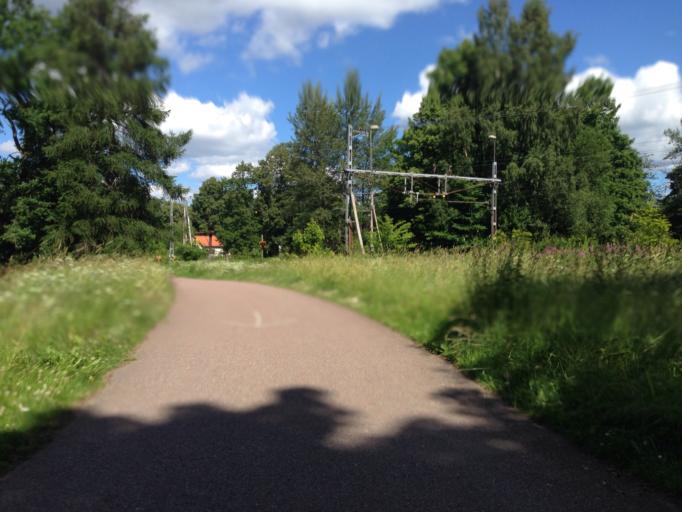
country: SE
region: Dalarna
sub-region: Ludvika Kommun
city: Ludvika
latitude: 60.1535
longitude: 15.1847
